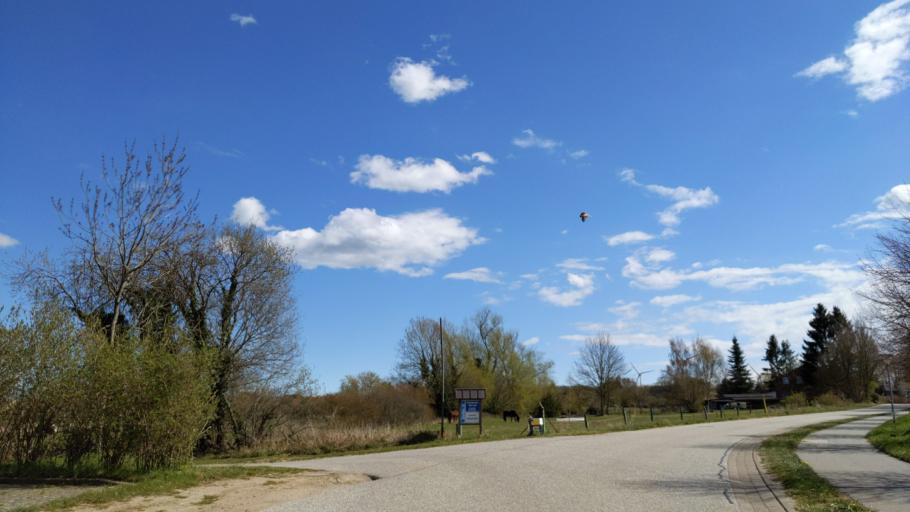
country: DE
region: Mecklenburg-Vorpommern
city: Selmsdorf
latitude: 53.8867
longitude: 10.8890
